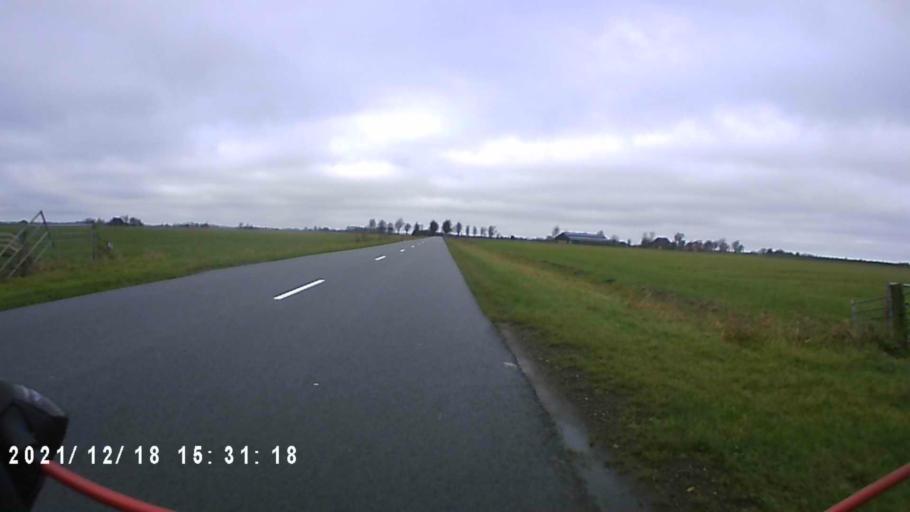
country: NL
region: Friesland
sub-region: Gemeente Dongeradeel
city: Anjum
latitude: 53.3391
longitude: 6.1373
